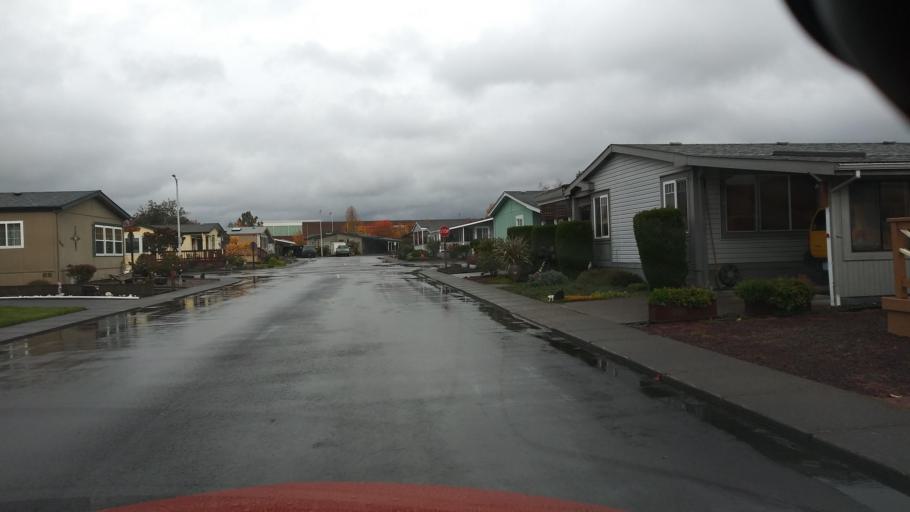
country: US
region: Oregon
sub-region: Washington County
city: Cornelius
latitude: 45.5125
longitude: -123.0724
